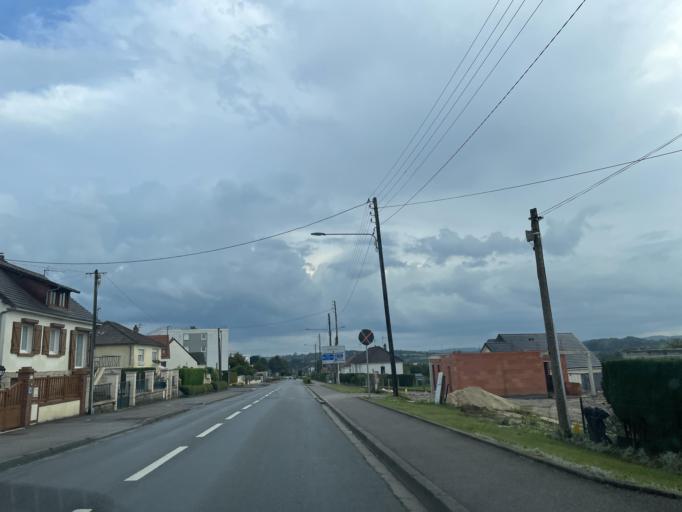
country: FR
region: Haute-Normandie
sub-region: Departement de la Seine-Maritime
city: Neufchatel-en-Bray
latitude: 49.7403
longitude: 1.4378
